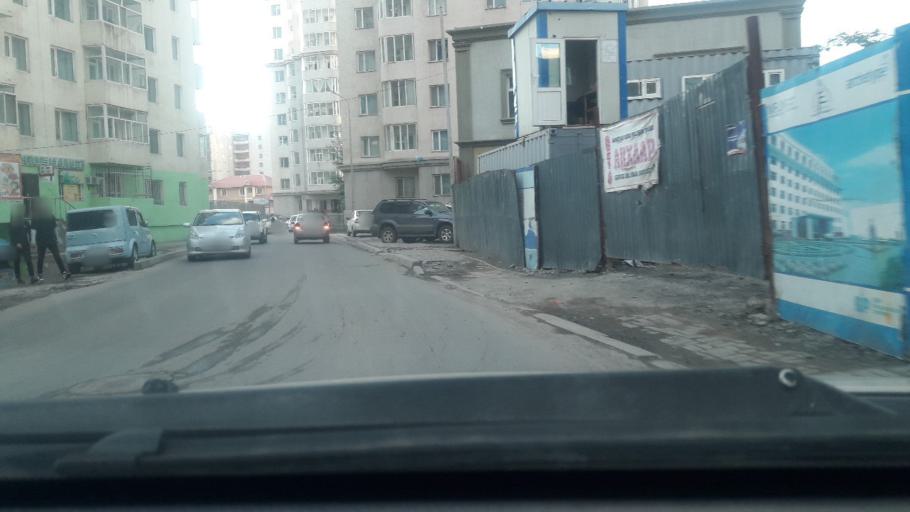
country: MN
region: Ulaanbaatar
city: Ulaanbaatar
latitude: 47.9112
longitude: 106.9342
